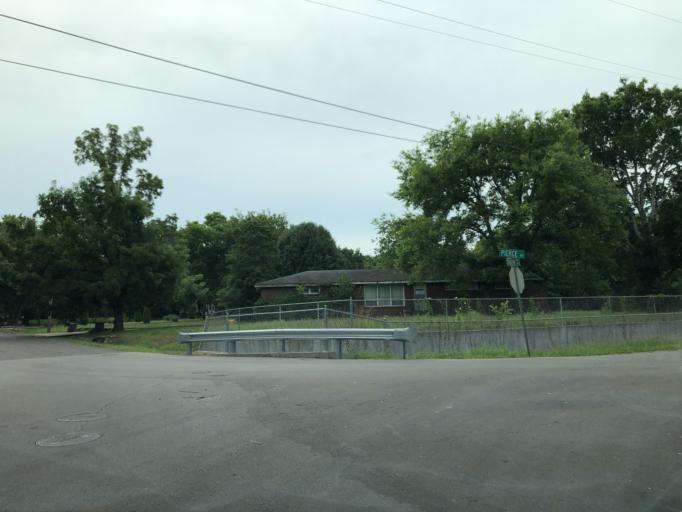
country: US
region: Tennessee
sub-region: Davidson County
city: Goodlettsville
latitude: 36.2795
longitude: -86.7022
